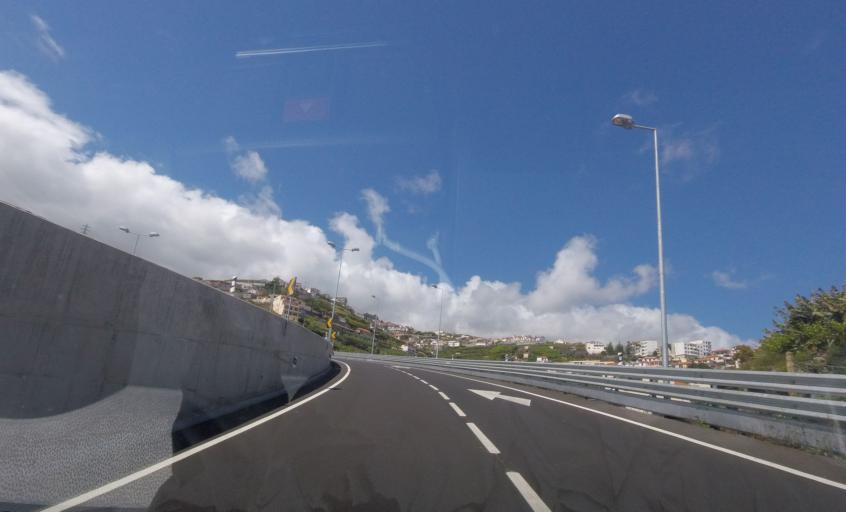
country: PT
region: Madeira
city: Camara de Lobos
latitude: 32.6613
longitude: -16.9677
